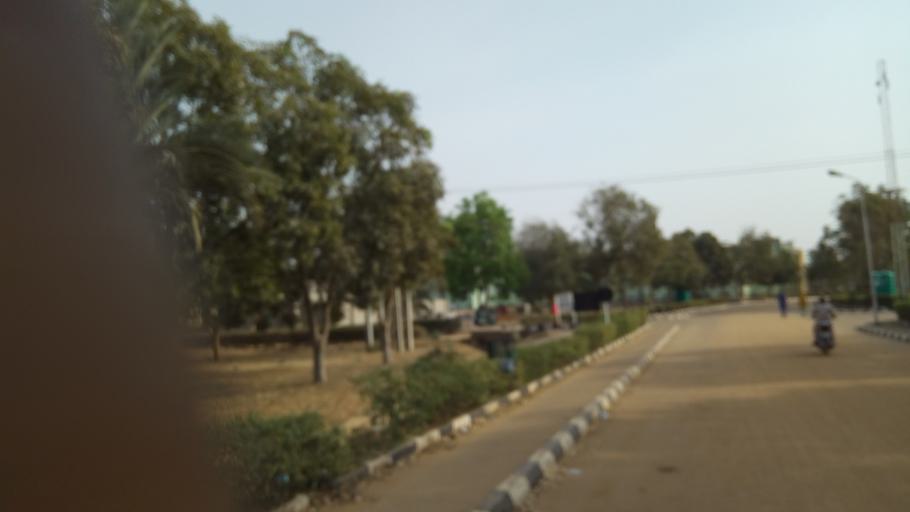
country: NG
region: Gombe
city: Gombe
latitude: 10.3065
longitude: 11.1750
